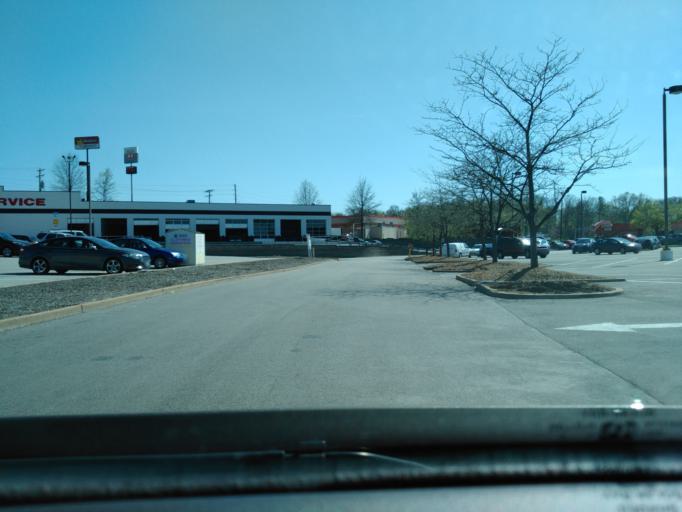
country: US
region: Missouri
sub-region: Saint Louis County
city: Concord
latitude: 38.4873
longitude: -90.3569
